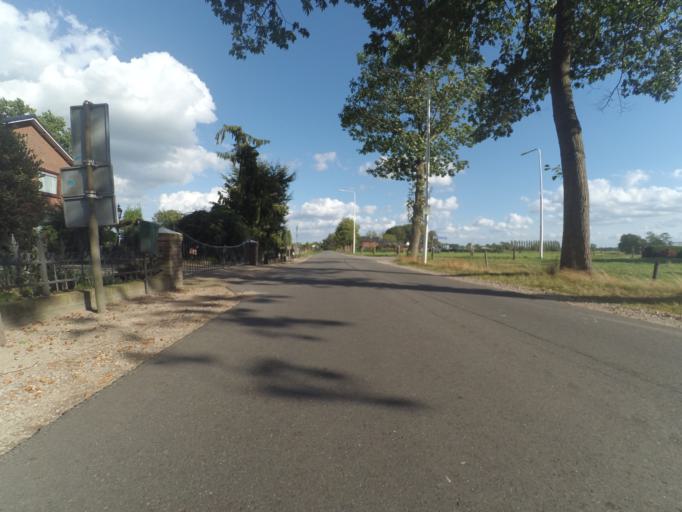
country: NL
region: Gelderland
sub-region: Gemeente Ede
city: Ederveen
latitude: 52.0890
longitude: 5.5698
